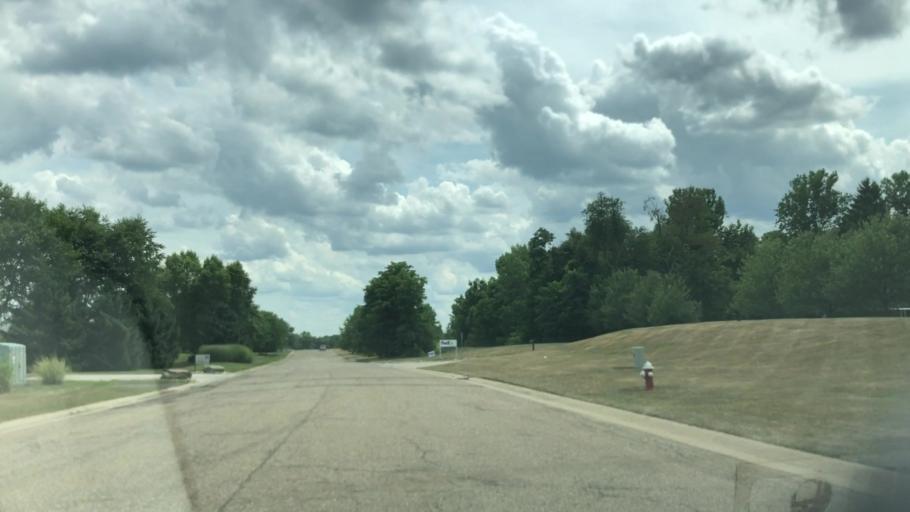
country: US
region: Ohio
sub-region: Summit County
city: Greensburg
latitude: 40.9044
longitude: -81.4461
